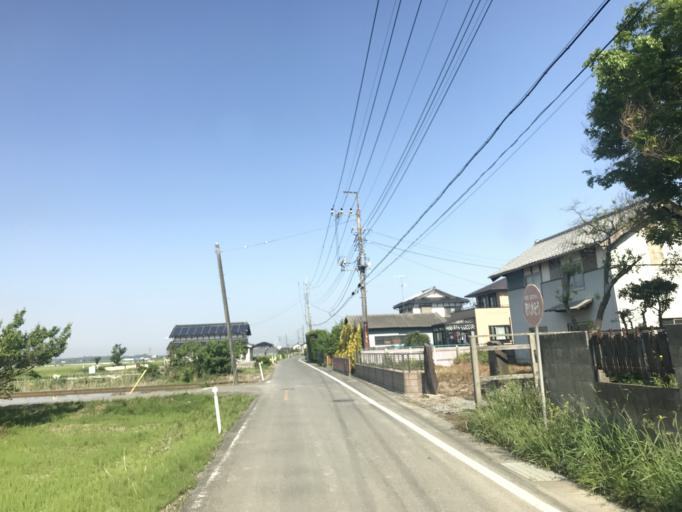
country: JP
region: Ibaraki
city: Mitsukaido
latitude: 36.0580
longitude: 140.0135
